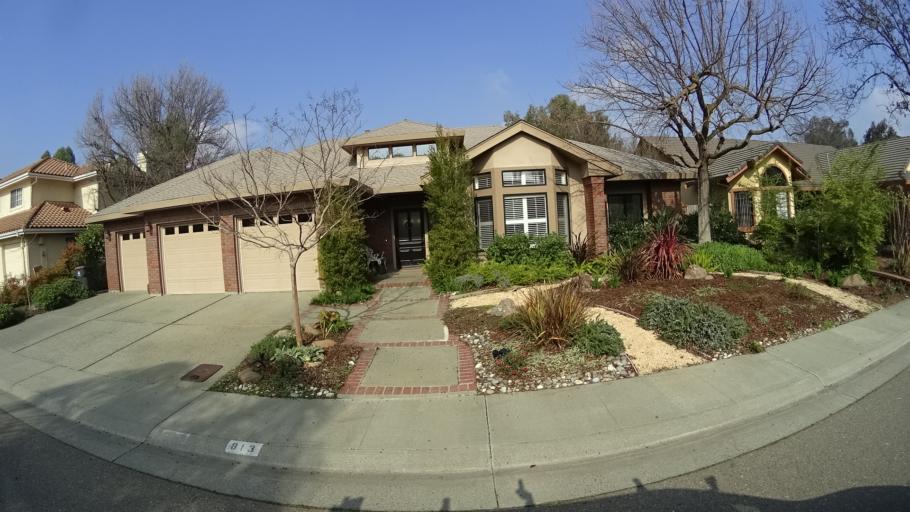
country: US
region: California
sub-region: Yolo County
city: Davis
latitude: 38.5711
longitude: -121.7596
